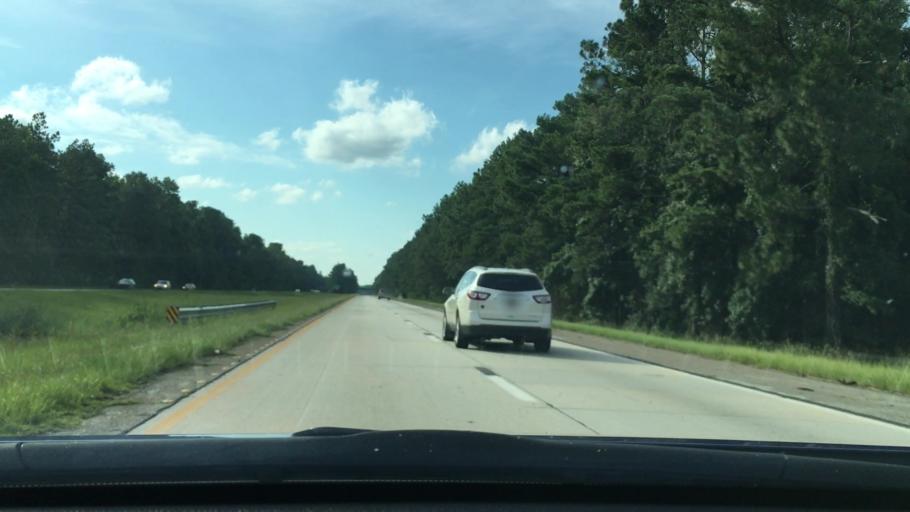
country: US
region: South Carolina
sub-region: Orangeburg County
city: Holly Hill
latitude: 33.2480
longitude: -80.4663
